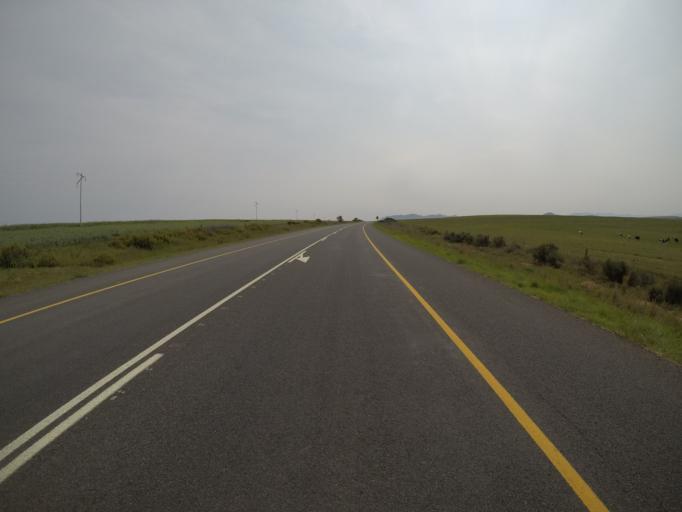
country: ZA
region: Western Cape
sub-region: West Coast District Municipality
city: Malmesbury
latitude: -33.5247
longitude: 18.8471
